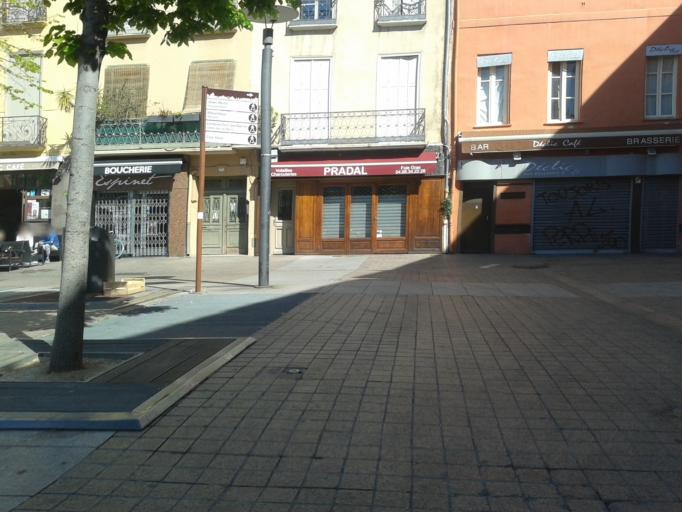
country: FR
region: Languedoc-Roussillon
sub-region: Departement des Pyrenees-Orientales
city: Perpignan
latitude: 42.6986
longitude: 2.8957
